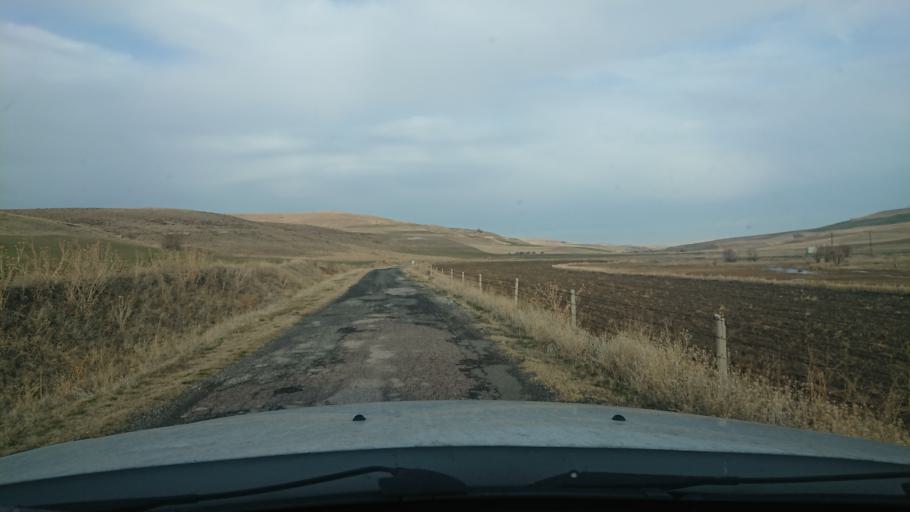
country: TR
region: Aksaray
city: Acipinar
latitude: 38.6800
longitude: 33.8652
